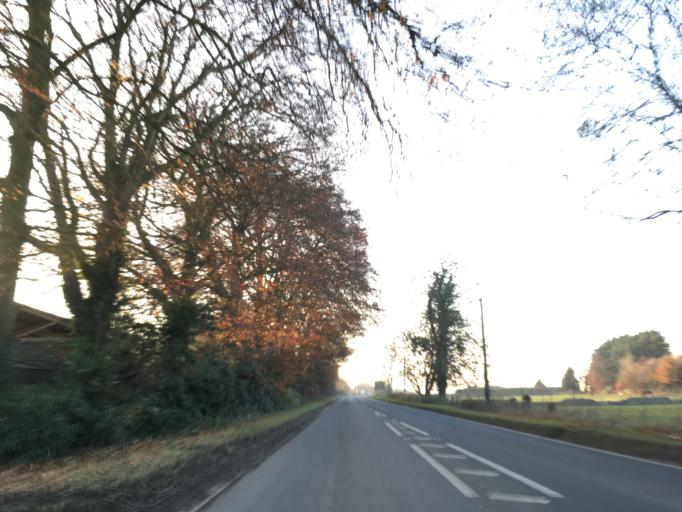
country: GB
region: England
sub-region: South Gloucestershire
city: Marshfield
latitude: 51.4635
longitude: -2.3019
